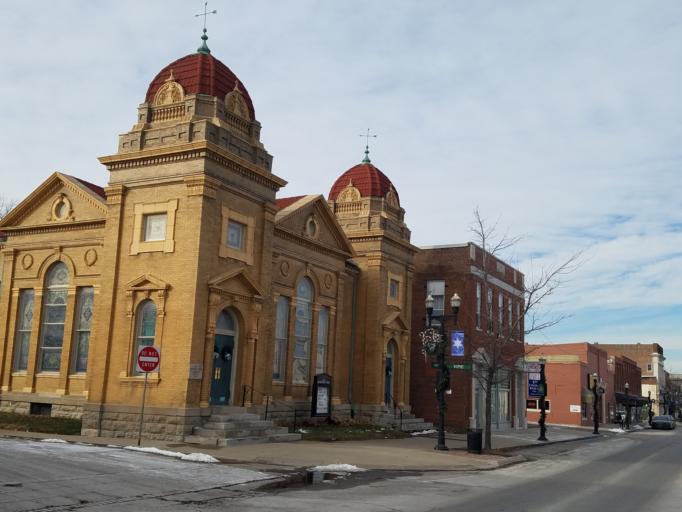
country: US
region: Missouri
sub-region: Cooper County
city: Boonville
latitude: 38.9733
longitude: -92.7429
